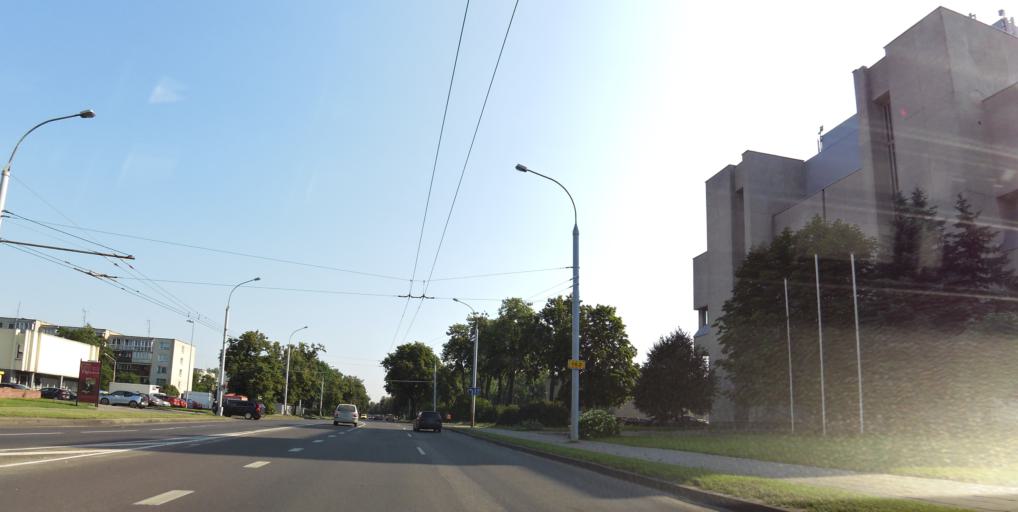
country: LT
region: Vilnius County
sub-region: Vilnius
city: Vilnius
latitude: 54.6966
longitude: 25.2996
